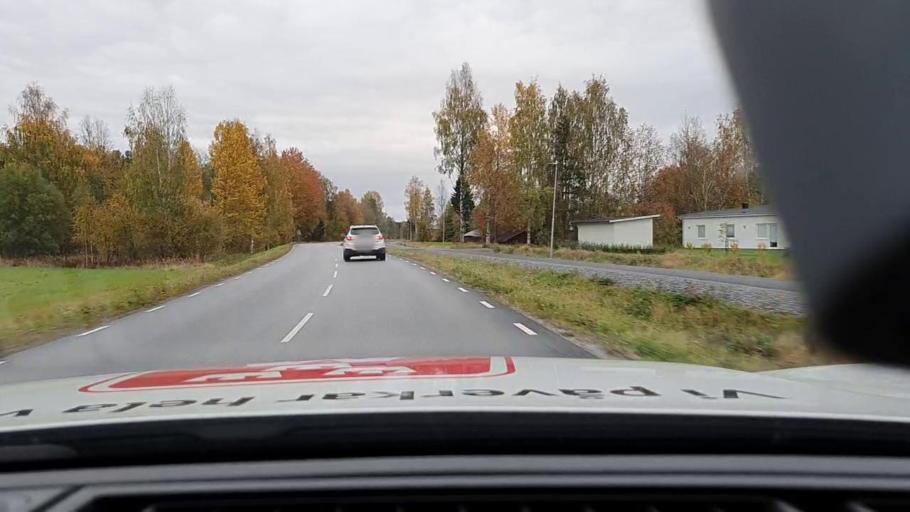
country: SE
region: Norrbotten
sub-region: Bodens Kommun
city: Saevast
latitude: 65.7710
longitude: 21.7027
